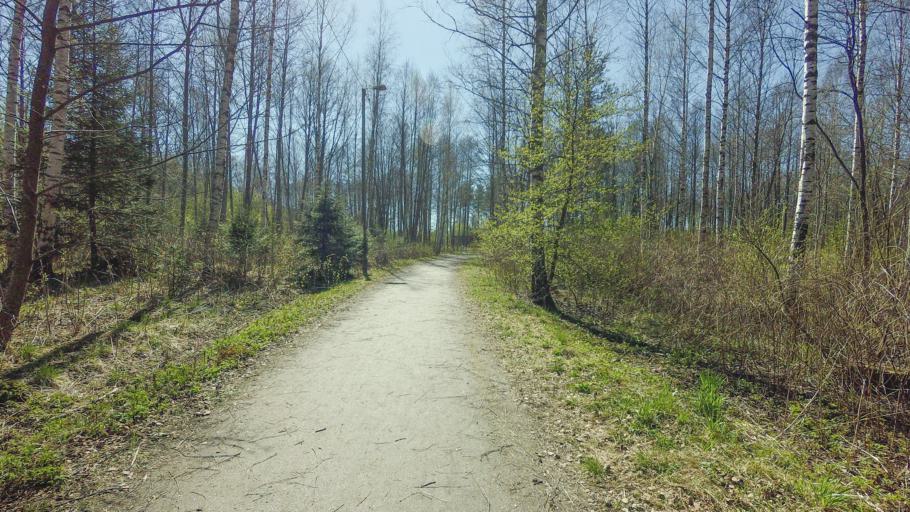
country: FI
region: Uusimaa
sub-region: Helsinki
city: Vantaa
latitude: 60.2238
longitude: 25.1309
